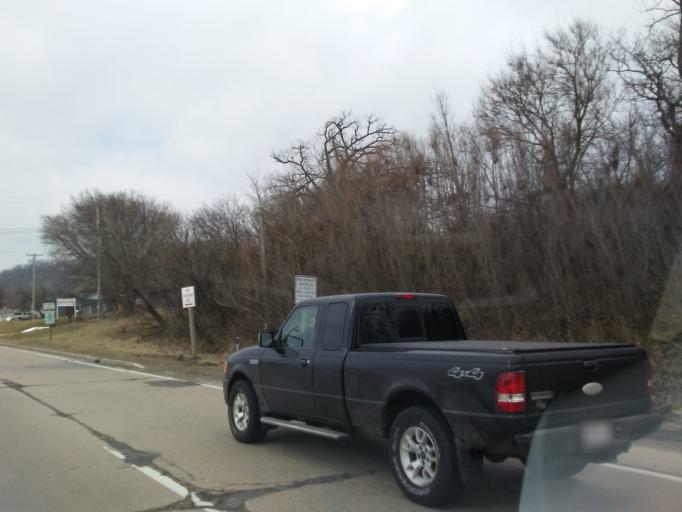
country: US
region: Wisconsin
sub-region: Richland County
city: Richland Center
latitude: 43.3170
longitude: -90.3561
